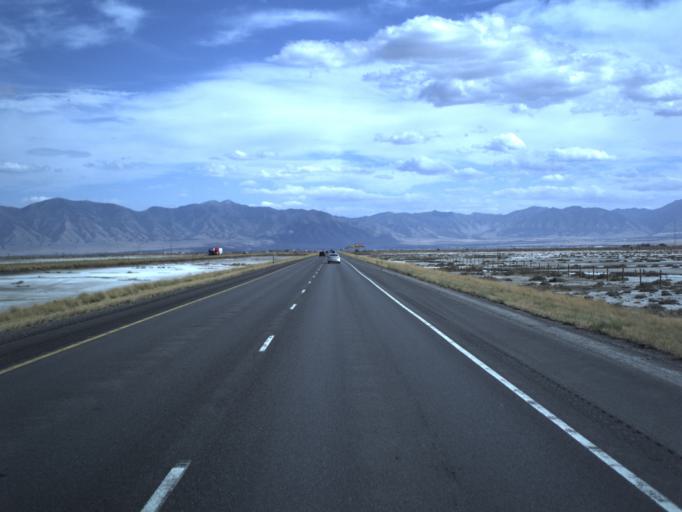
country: US
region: Utah
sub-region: Tooele County
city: Grantsville
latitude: 40.6960
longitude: -112.4767
